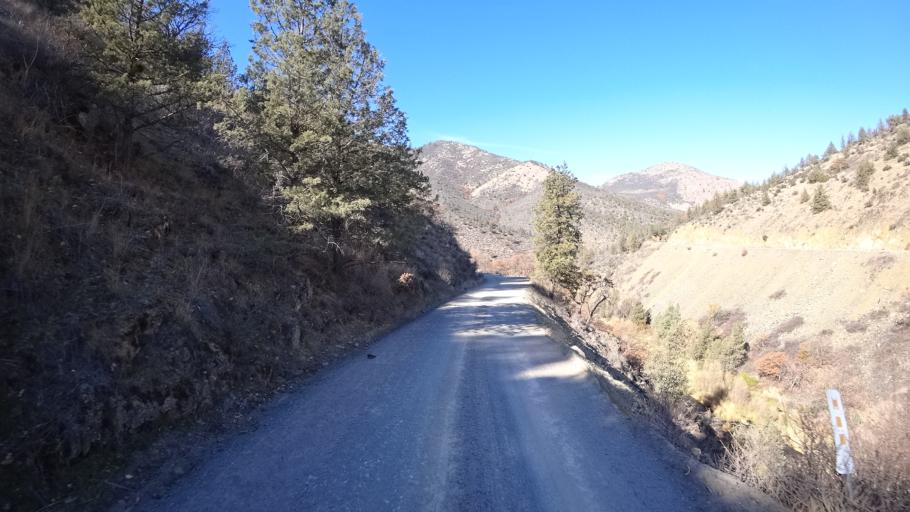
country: US
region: California
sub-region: Siskiyou County
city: Yreka
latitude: 41.7895
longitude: -122.6074
